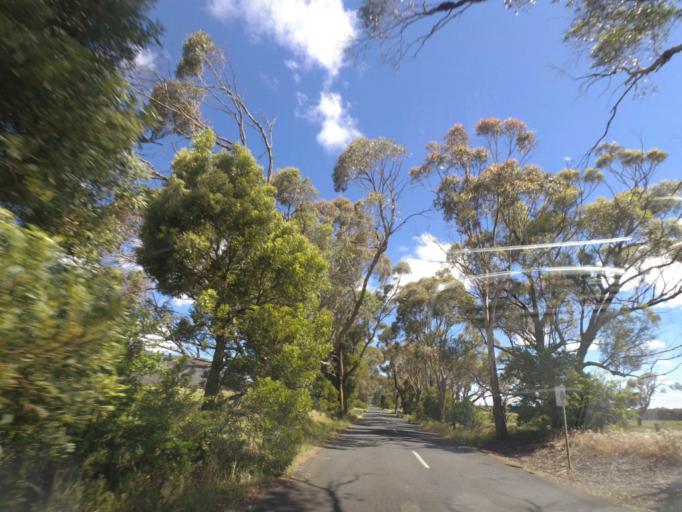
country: AU
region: Victoria
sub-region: Hume
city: Sunbury
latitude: -37.3416
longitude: 144.5570
